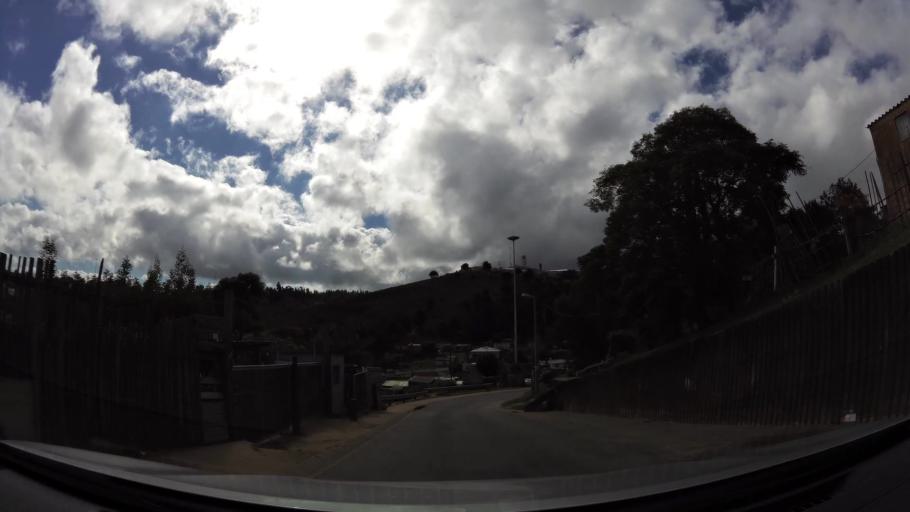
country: ZA
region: Western Cape
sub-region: Eden District Municipality
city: Knysna
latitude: -34.0345
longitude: 23.1035
